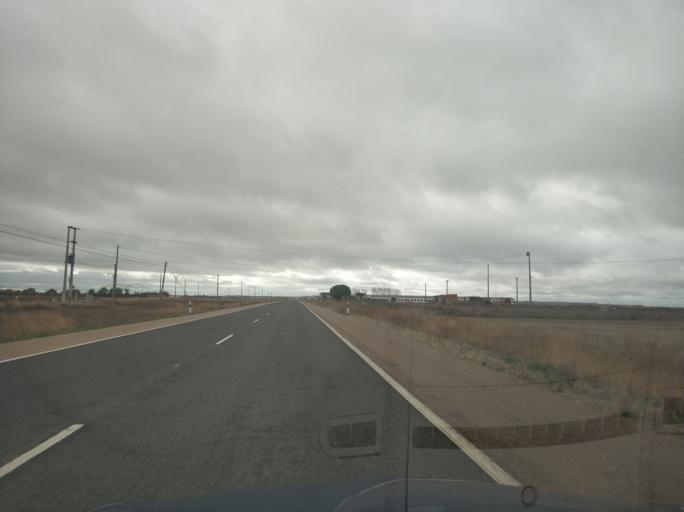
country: ES
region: Castille and Leon
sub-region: Provincia de Salamanca
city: Pedrosillo el Ralo
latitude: 41.0418
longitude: -5.5681
